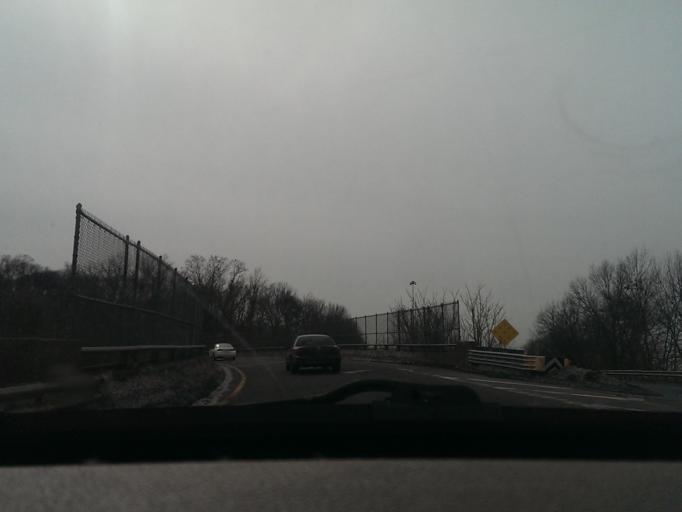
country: US
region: Massachusetts
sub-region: Hampden County
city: Longmeadow
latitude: 42.0755
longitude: -72.5827
